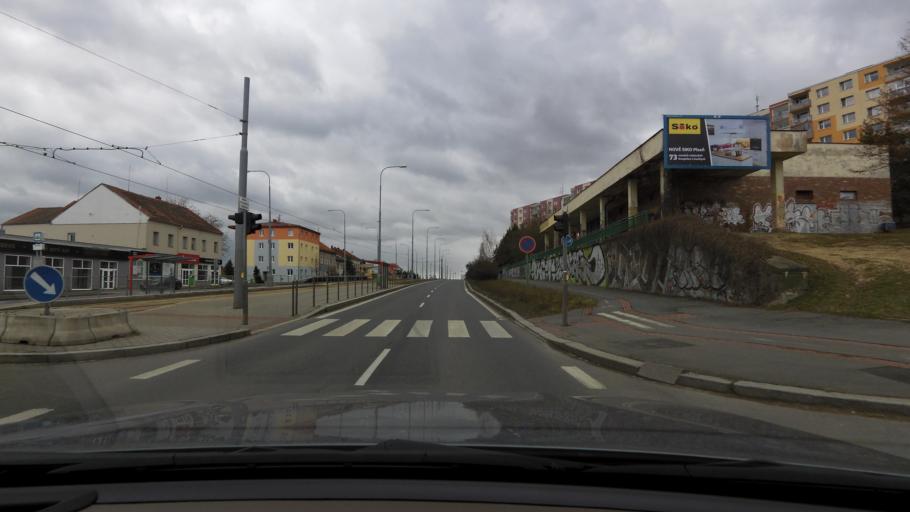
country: CZ
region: Plzensky
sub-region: Okres Plzen-Mesto
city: Pilsen
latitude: 49.7716
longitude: 13.3769
